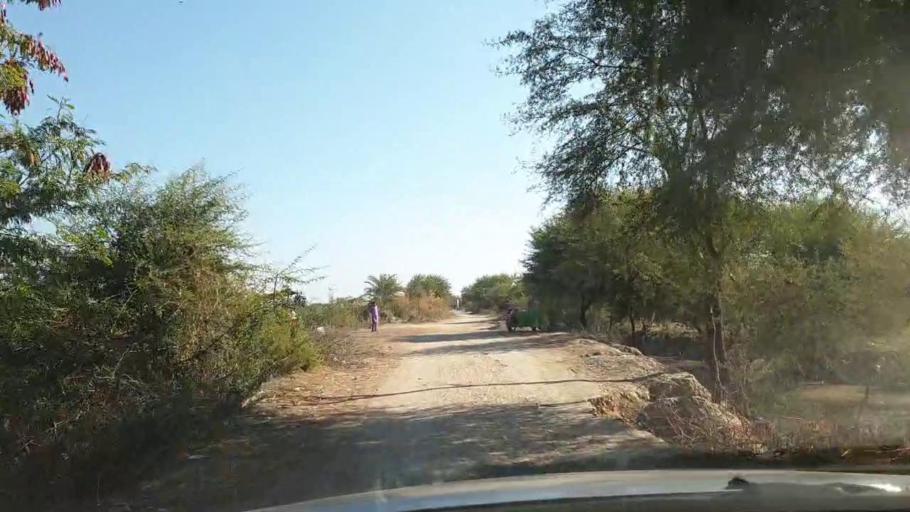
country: PK
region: Sindh
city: Jhol
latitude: 25.9180
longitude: 68.9637
